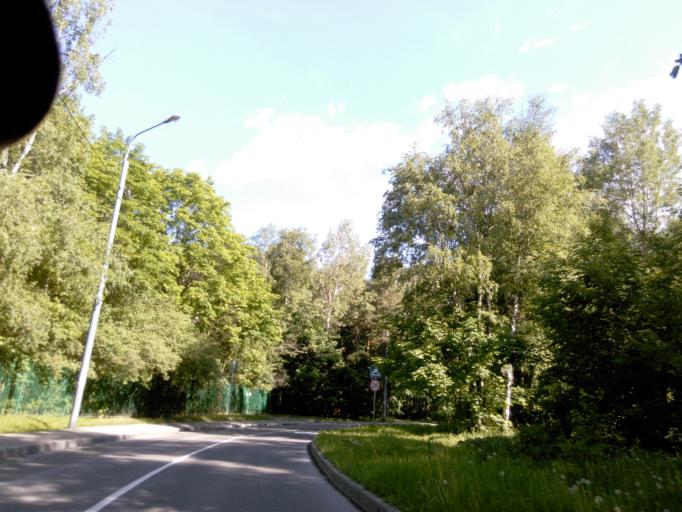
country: RU
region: Moscow
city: Zelenograd
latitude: 56.0036
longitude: 37.2009
